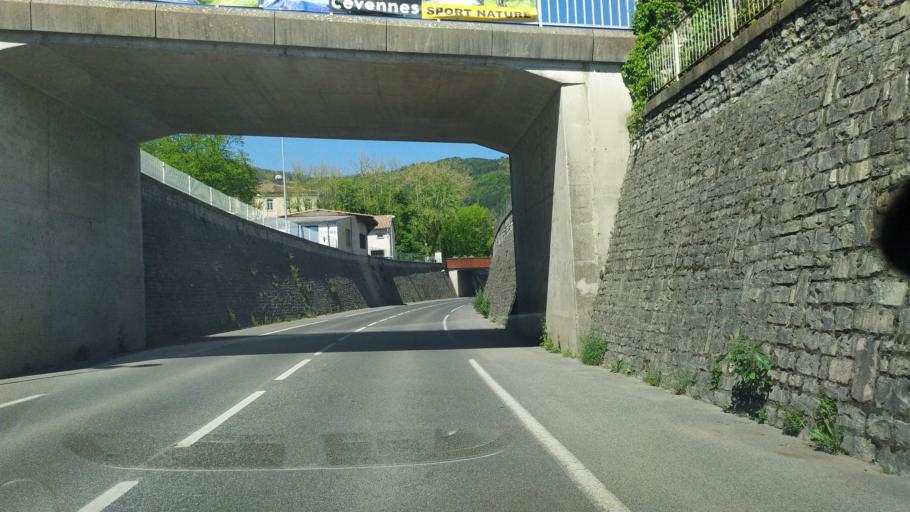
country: FR
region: Languedoc-Roussillon
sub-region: Departement du Gard
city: Le Vigan
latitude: 43.9886
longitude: 3.6050
